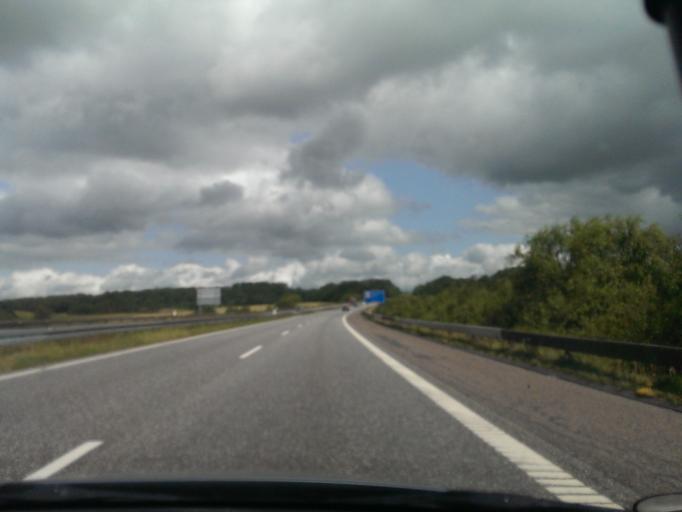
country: DK
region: North Denmark
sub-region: Mariagerfjord Kommune
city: Hobro
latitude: 56.6155
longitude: 9.7354
